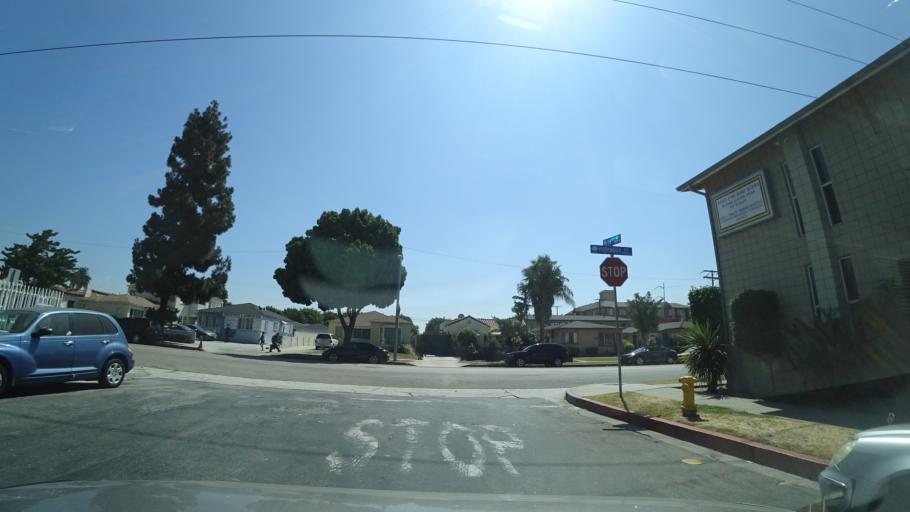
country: US
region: California
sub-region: Los Angeles County
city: Lennox
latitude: 33.9463
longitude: -118.3616
